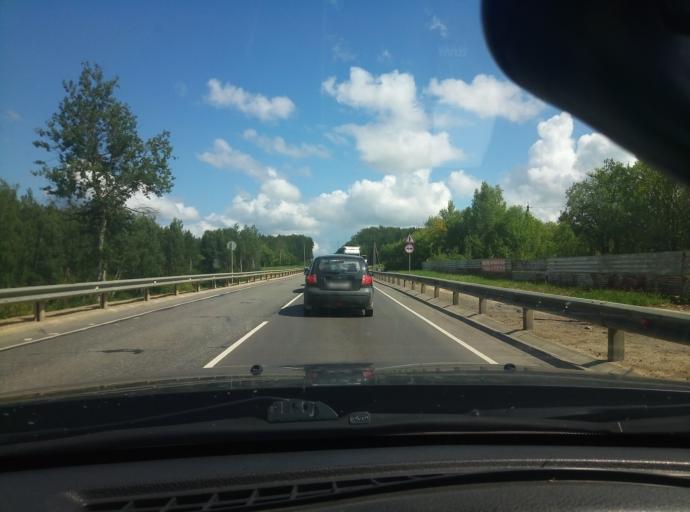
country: RU
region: Tula
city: Novogurovskiy
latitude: 54.2799
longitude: 37.2100
